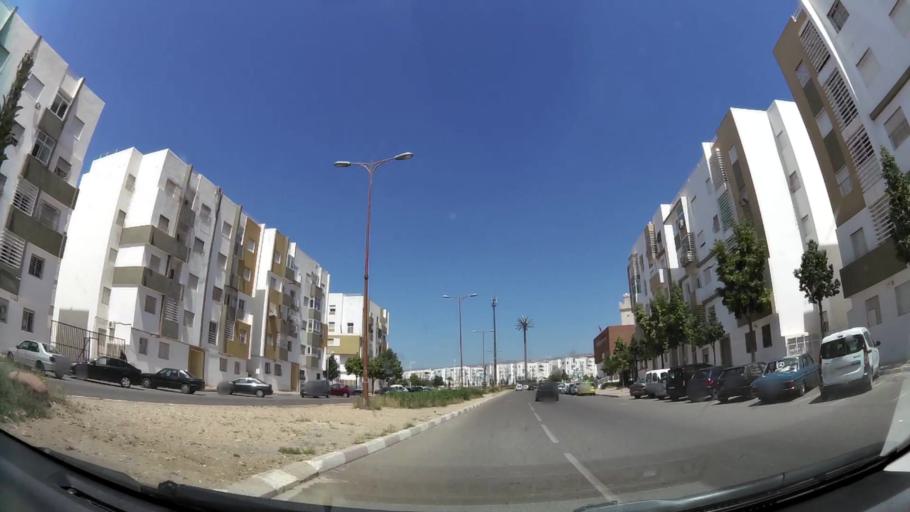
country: MA
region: Oued ed Dahab-Lagouira
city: Dakhla
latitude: 30.4325
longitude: -9.5568
